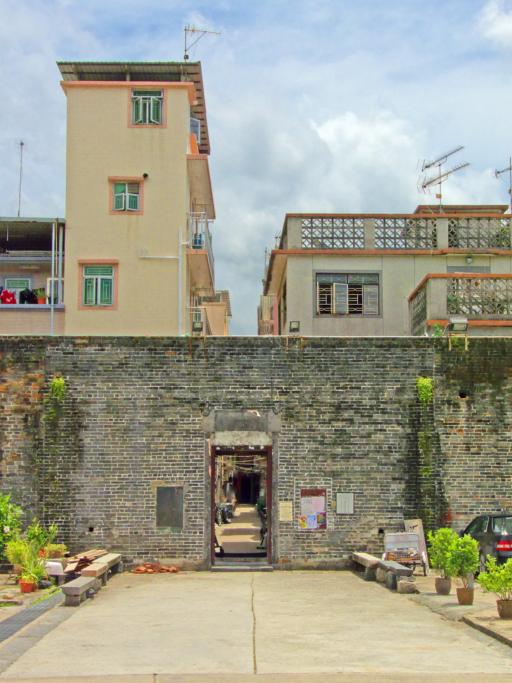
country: HK
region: Yuen Long
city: Yuen Long Kau Hui
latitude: 22.4396
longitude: 114.0634
